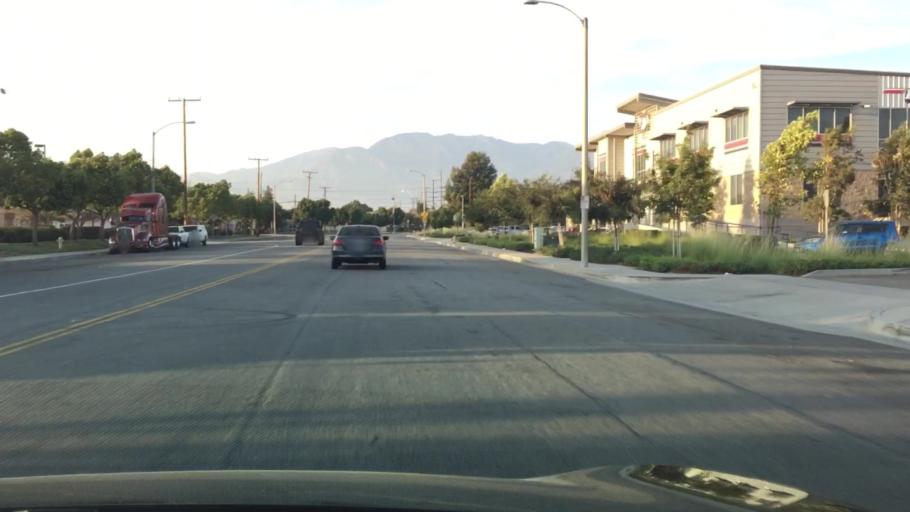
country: US
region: California
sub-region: San Bernardino County
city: Ontario
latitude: 34.0487
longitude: -117.6416
